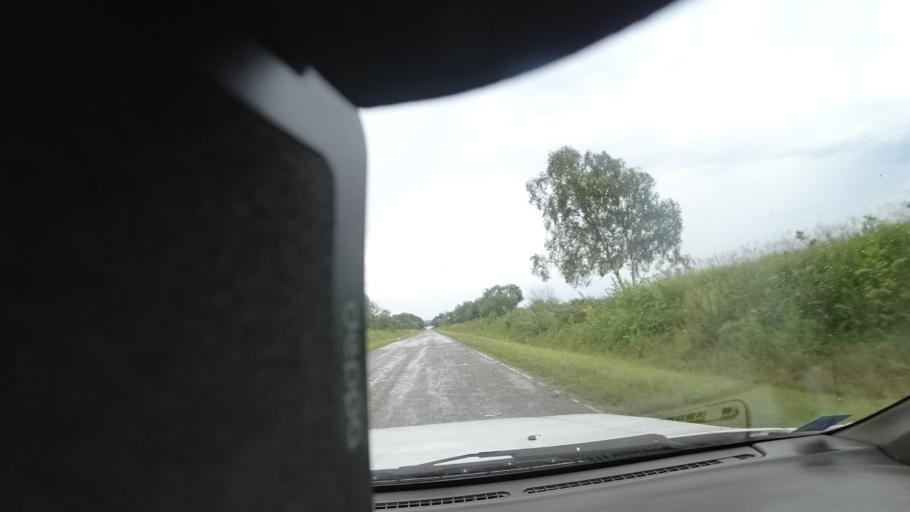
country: RU
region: Primorskiy
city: Lazo
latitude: 45.8701
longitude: 133.7124
